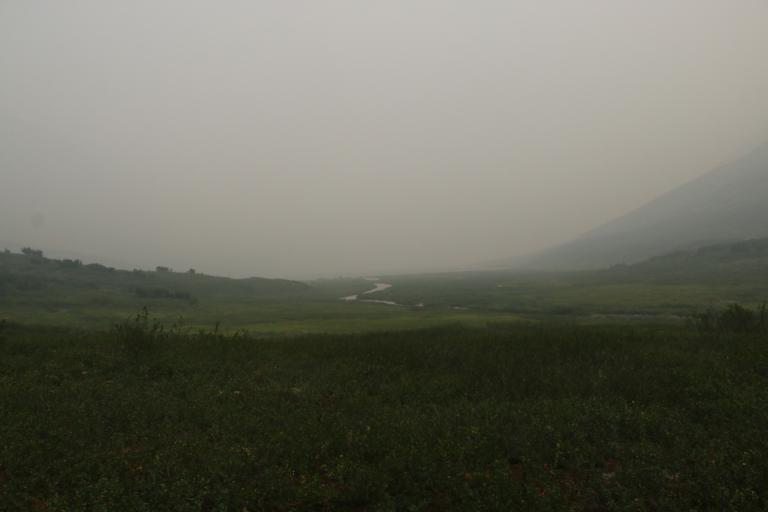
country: RU
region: Respublika Buryatiya
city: Kichera
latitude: 56.2447
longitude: 110.7885
